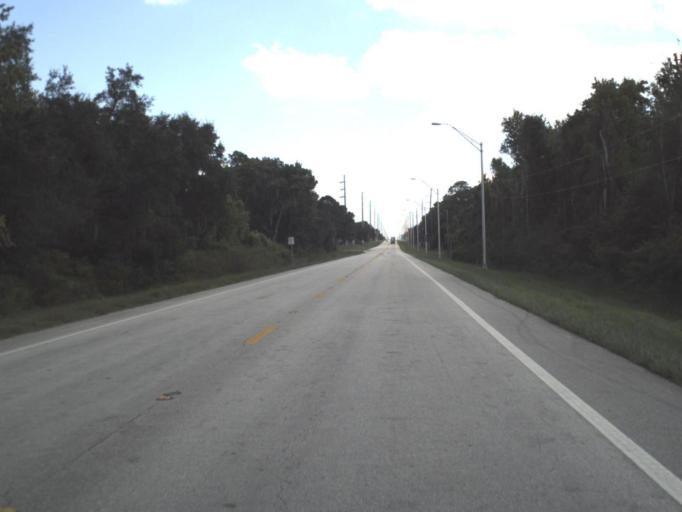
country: US
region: Florida
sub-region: Highlands County
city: Sebring
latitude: 27.4124
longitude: -81.5185
